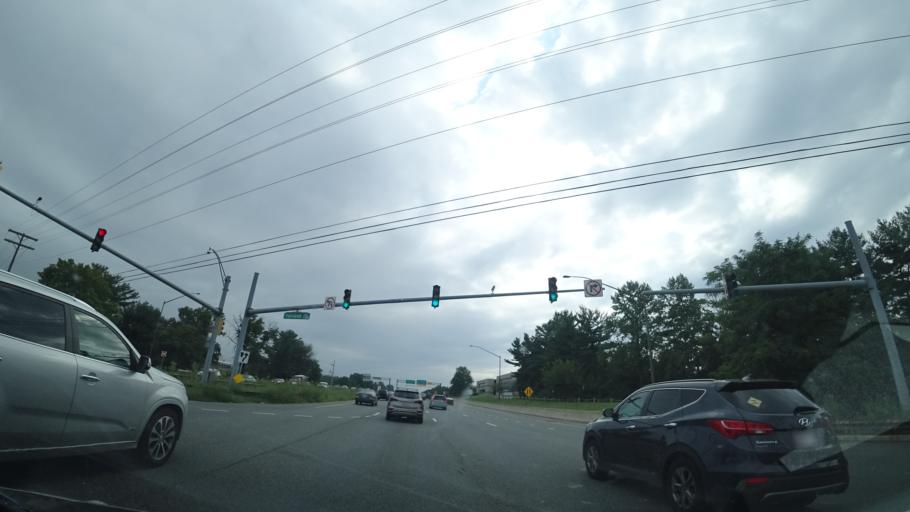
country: US
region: Maryland
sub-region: Montgomery County
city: Fairland
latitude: 39.0735
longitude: -76.9559
